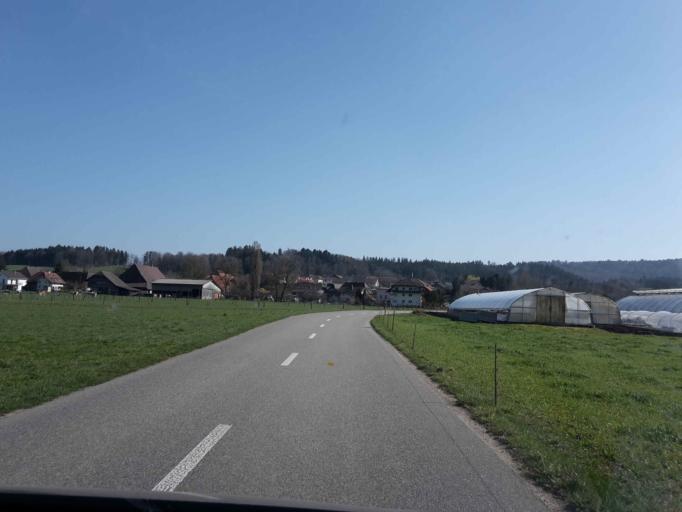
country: CH
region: Bern
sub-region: Oberaargau
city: Lotzwil
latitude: 47.1876
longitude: 7.7515
